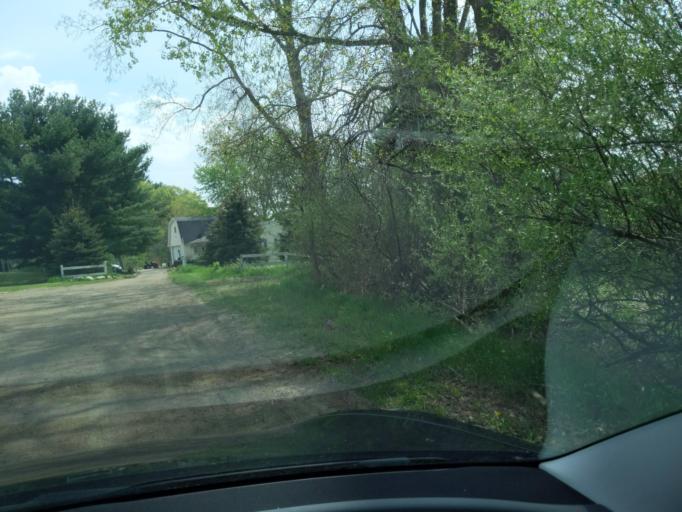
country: US
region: Michigan
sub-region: Ingham County
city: Stockbridge
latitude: 42.4405
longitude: -84.0700
